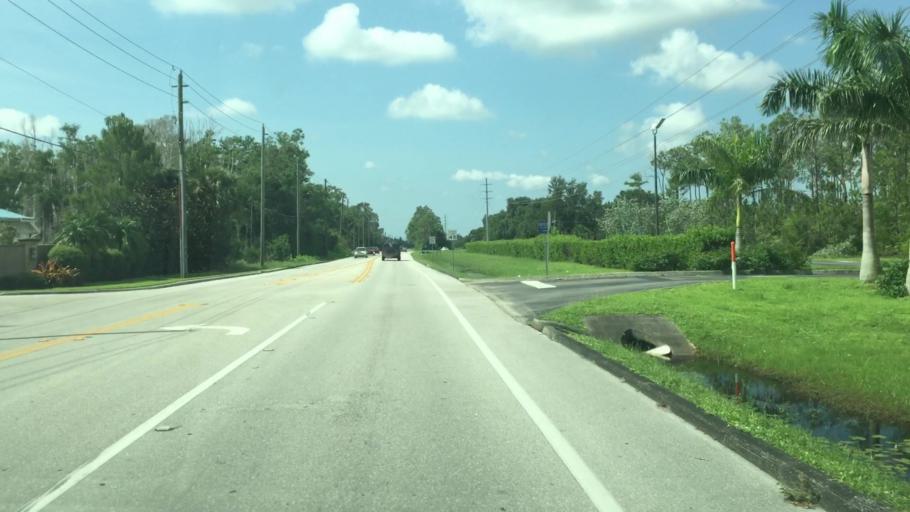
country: US
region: Florida
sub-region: Lee County
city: Villas
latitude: 26.5609
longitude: -81.8469
